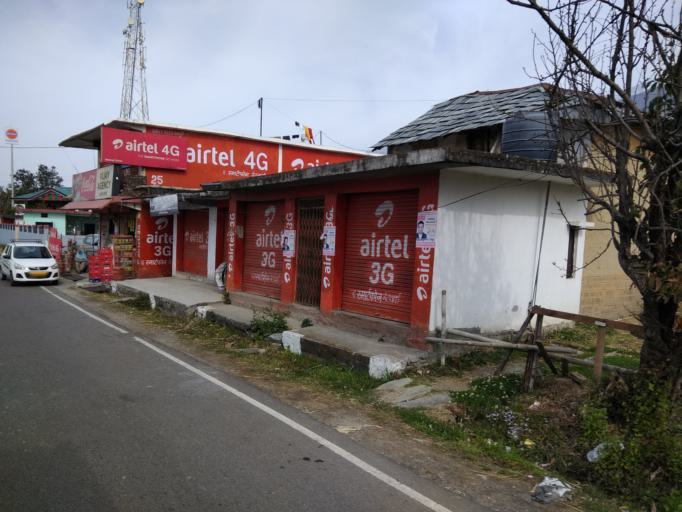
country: IN
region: Himachal Pradesh
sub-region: Kangra
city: Dharmsala
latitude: 32.1644
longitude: 76.3977
